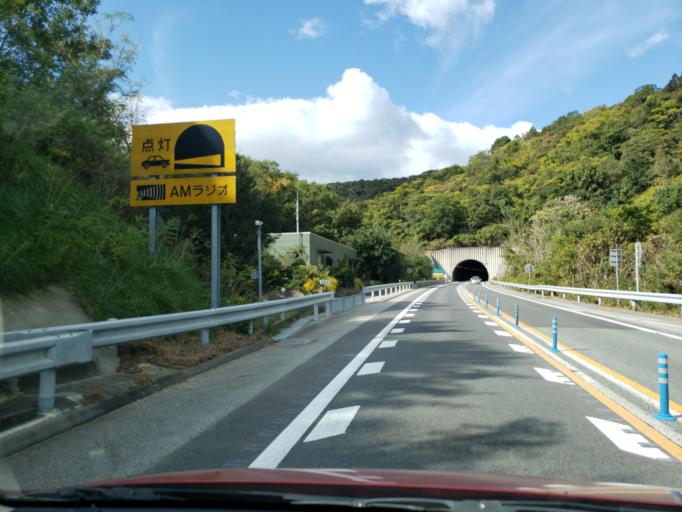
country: JP
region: Tokushima
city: Kamojimacho-jogejima
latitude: 34.1049
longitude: 134.2958
